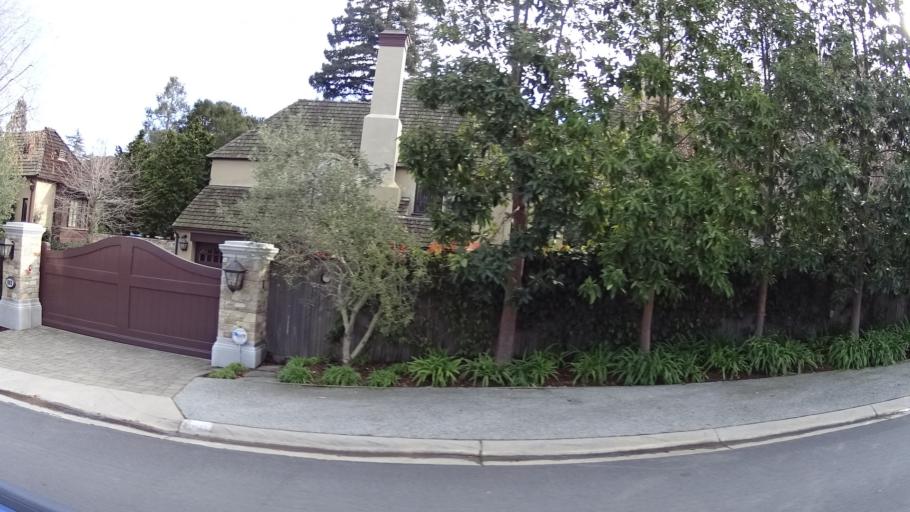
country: US
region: California
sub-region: San Mateo County
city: Burlingame
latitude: 37.5681
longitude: -122.3565
